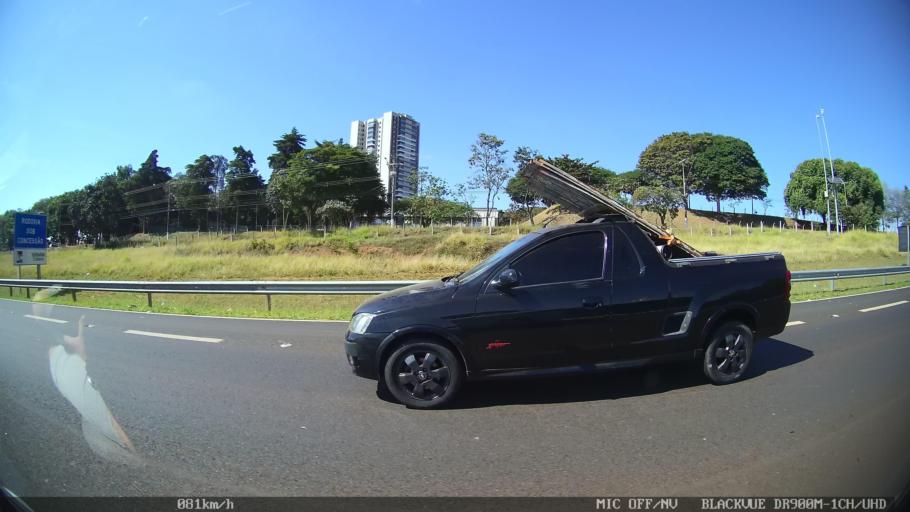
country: BR
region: Sao Paulo
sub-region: Franca
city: Franca
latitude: -20.5586
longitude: -47.4090
